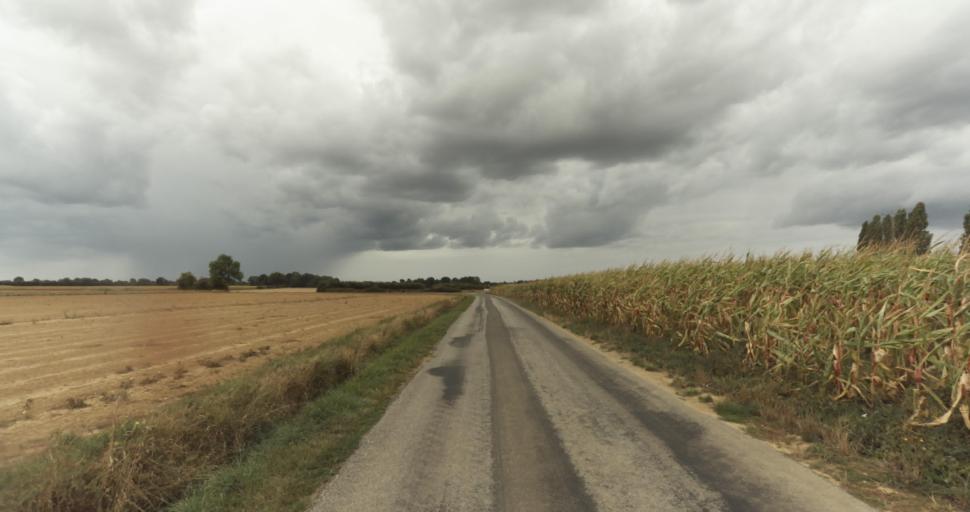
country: FR
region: Lower Normandy
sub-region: Departement du Calvados
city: Orbec
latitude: 48.9125
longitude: 0.3676
